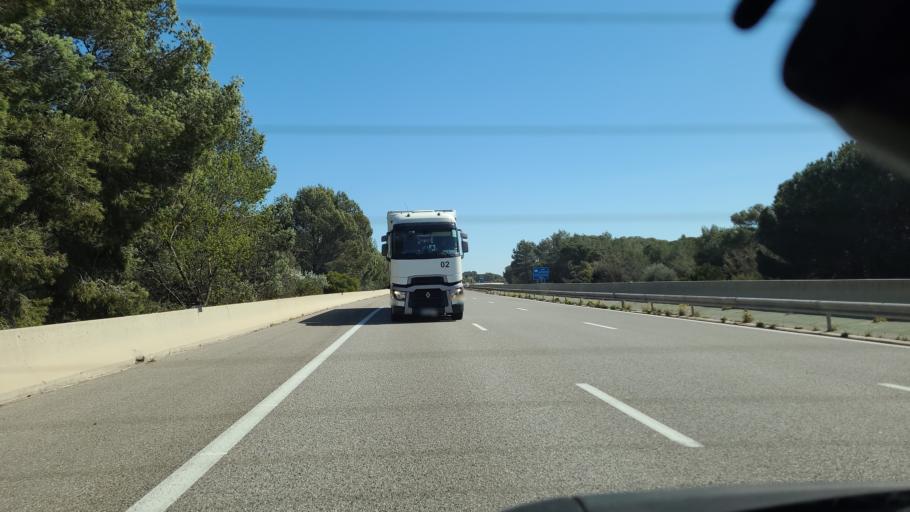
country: FR
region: Provence-Alpes-Cote d'Azur
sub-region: Departement du Var
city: Puget-sur-Argens
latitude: 43.4673
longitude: 6.6650
